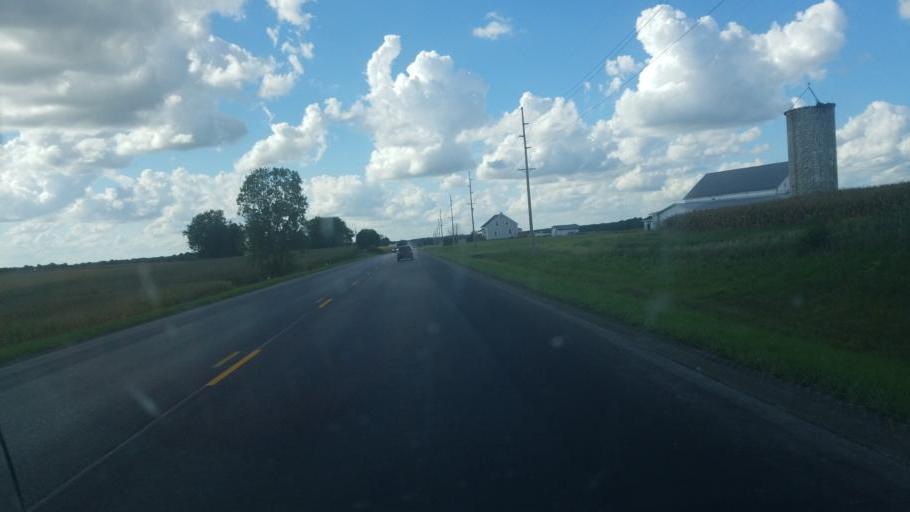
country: US
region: Ohio
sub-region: Hardin County
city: Kenton
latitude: 40.6614
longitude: -83.6464
